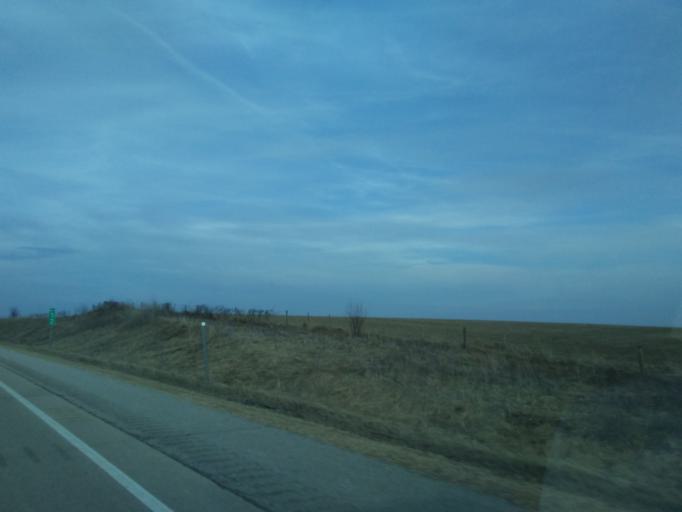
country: US
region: Wisconsin
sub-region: Iowa County
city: Dodgeville
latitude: 42.9818
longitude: -90.0159
